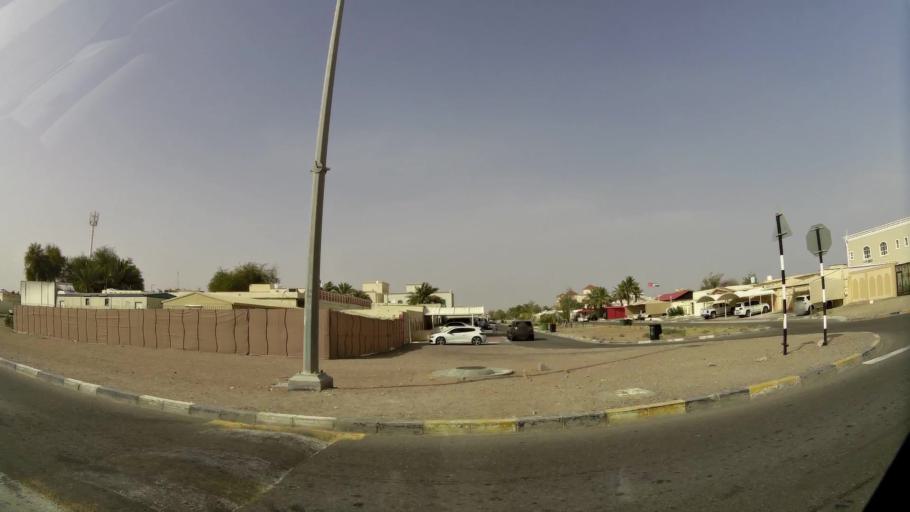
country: AE
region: Abu Dhabi
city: Al Ain
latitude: 24.2099
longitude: 55.5869
